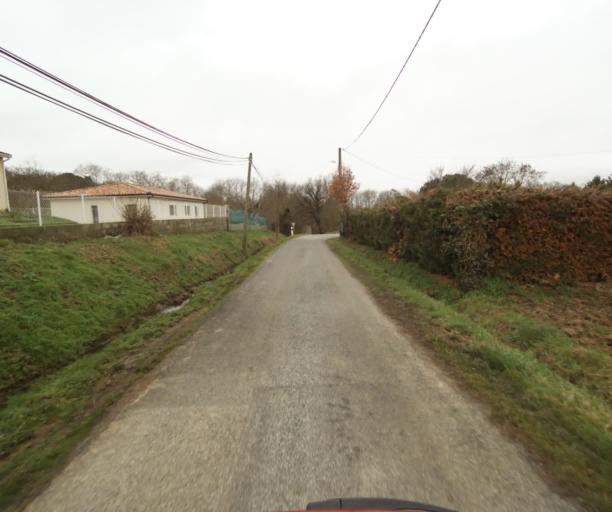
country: FR
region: Midi-Pyrenees
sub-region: Departement de la Haute-Garonne
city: Gaillac-Toulza
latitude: 43.2627
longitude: 1.5155
